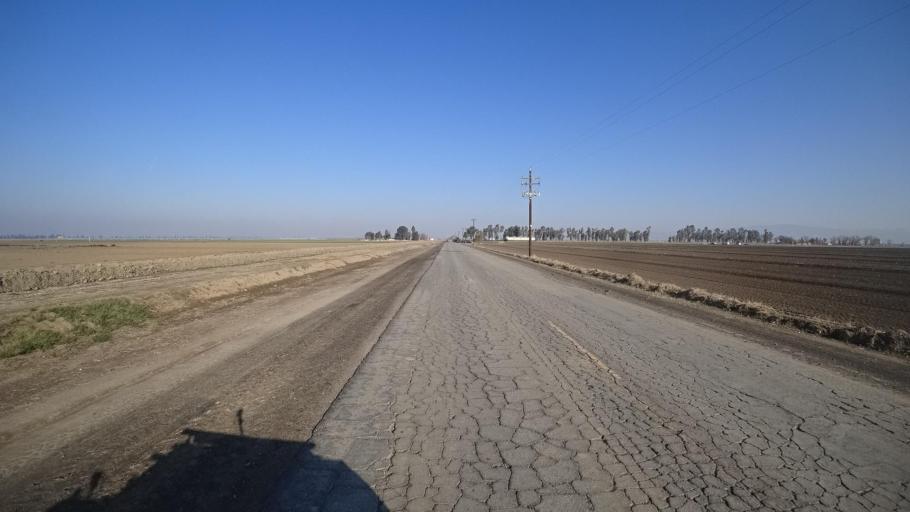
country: US
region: California
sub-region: Kern County
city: Weedpatch
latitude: 35.1810
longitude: -118.9678
